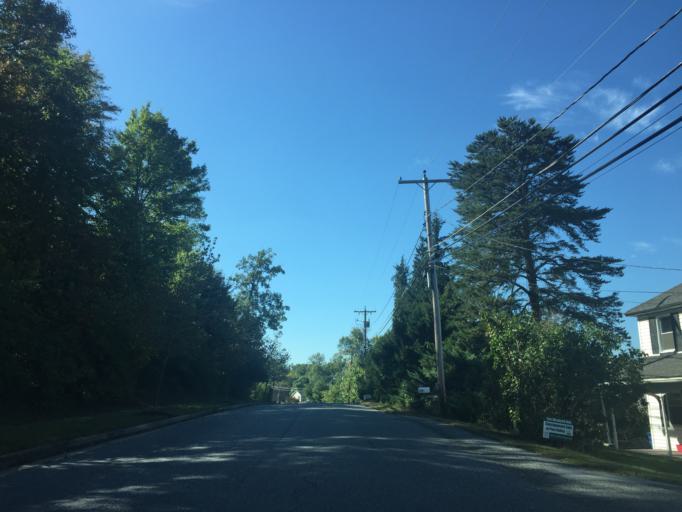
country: US
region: Maryland
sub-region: Baltimore County
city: Overlea
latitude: 39.3787
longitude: -76.4892
